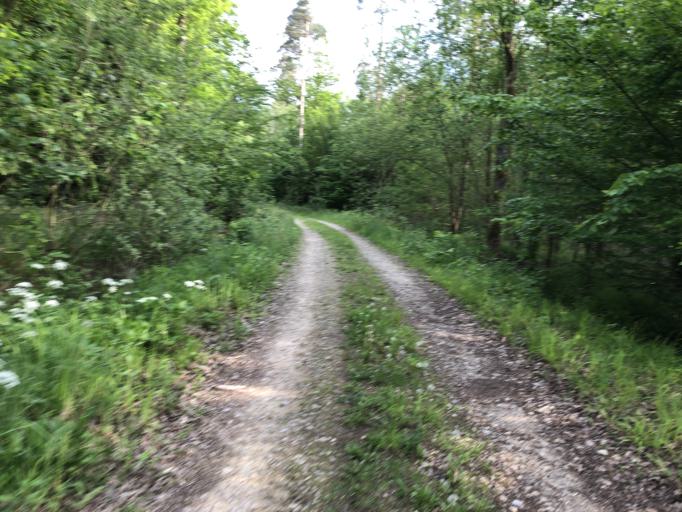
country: DE
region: Bavaria
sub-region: Upper Franconia
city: Memmelsdorf
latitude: 49.9230
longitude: 10.9517
